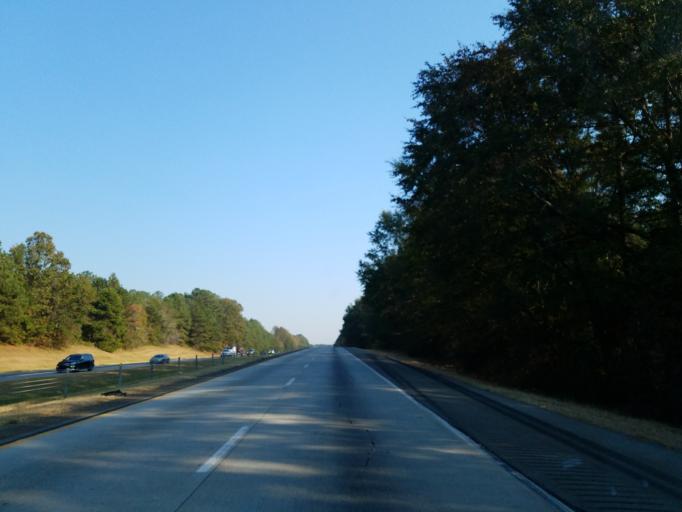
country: US
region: Georgia
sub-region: Bibb County
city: West Point
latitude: 32.9462
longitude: -83.7950
